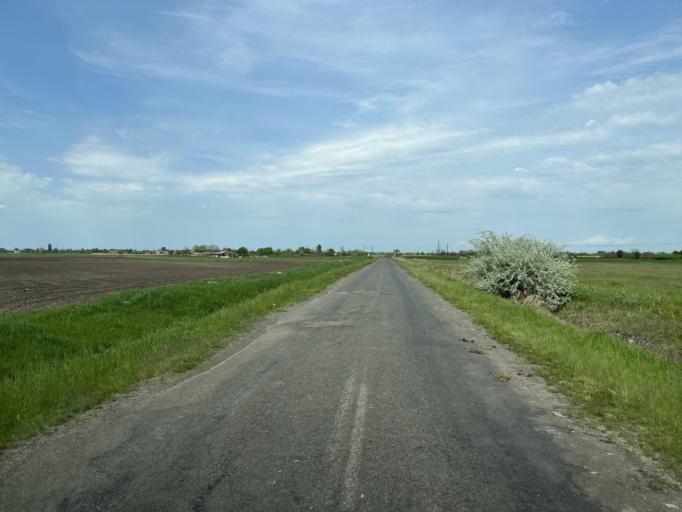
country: HU
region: Pest
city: Tapiogyorgye
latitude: 47.3160
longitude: 19.9705
